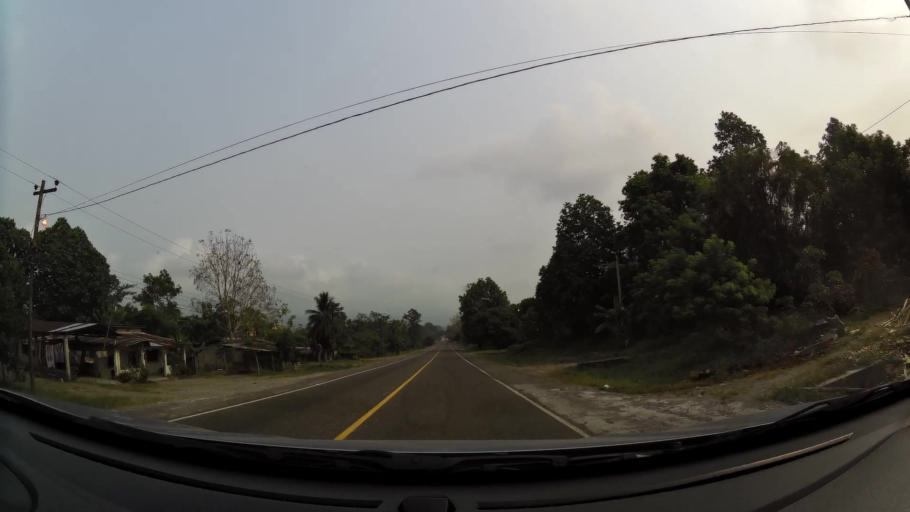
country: HN
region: Atlantida
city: Mezapa
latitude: 15.5985
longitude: -87.6093
